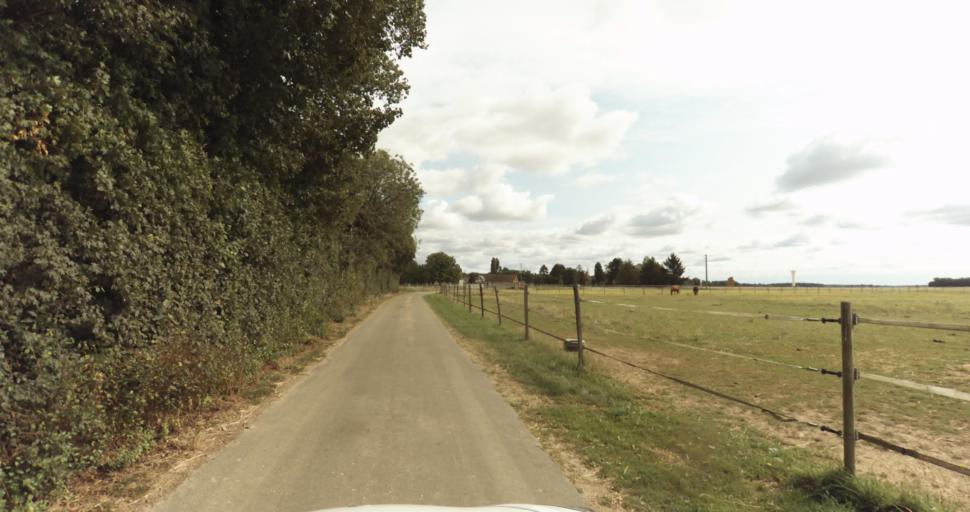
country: FR
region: Haute-Normandie
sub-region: Departement de l'Eure
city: Tillieres-sur-Avre
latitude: 48.7931
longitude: 1.0976
